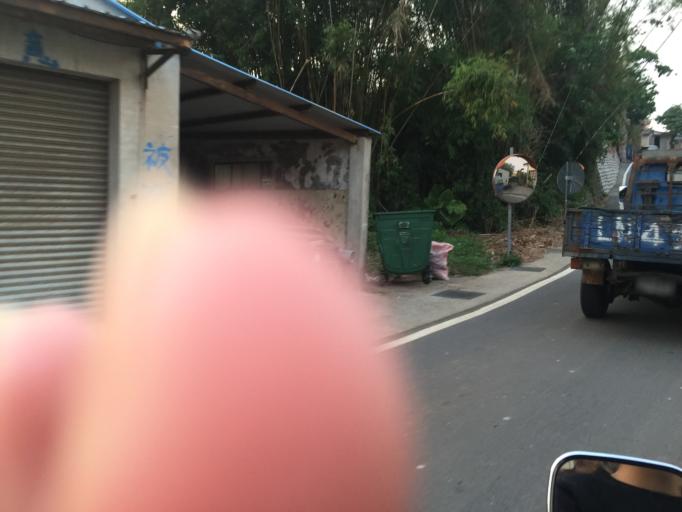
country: TW
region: Taiwan
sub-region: Miaoli
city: Miaoli
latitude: 24.4758
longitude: 120.7773
